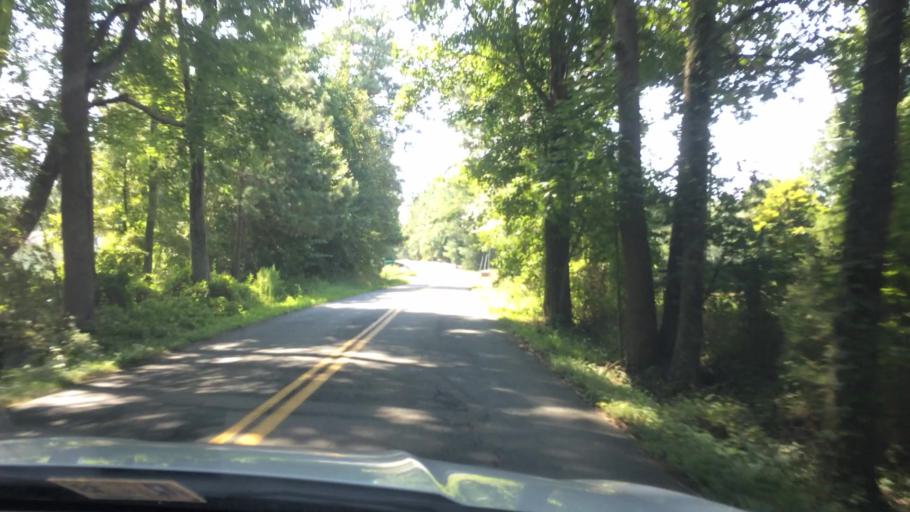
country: US
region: Virginia
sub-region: Henrico County
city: Sandston
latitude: 37.5154
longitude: -77.1617
